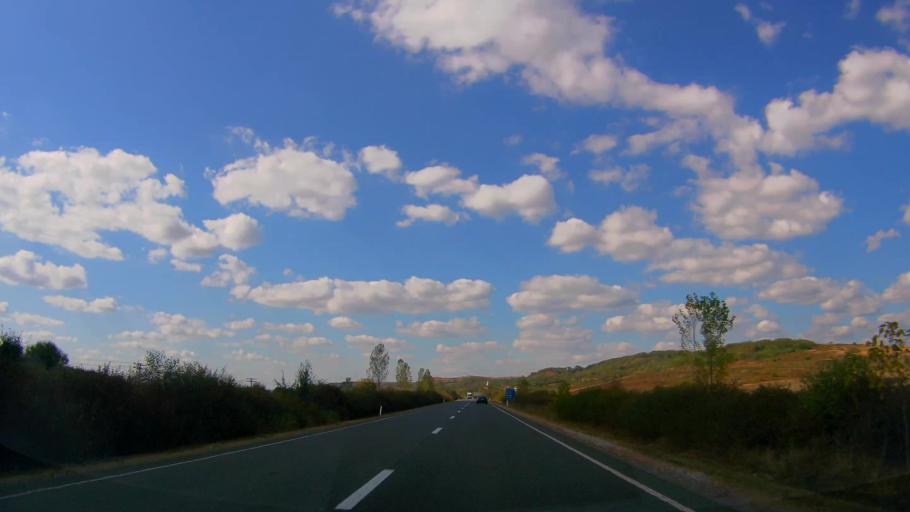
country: RO
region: Salaj
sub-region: Comuna Bocsa
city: Bocsa
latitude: 47.3100
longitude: 22.9172
